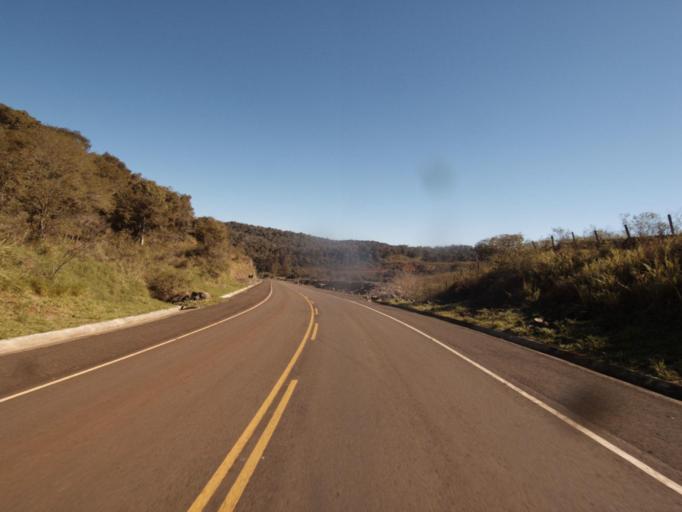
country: AR
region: Misiones
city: Bernardo de Irigoyen
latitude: -26.6093
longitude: -53.7289
